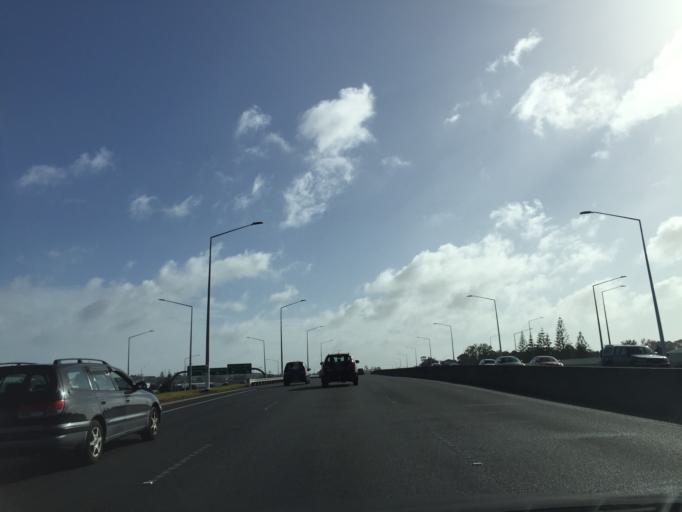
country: NZ
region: Auckland
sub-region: Auckland
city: North Shore
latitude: -36.7740
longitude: 174.7438
